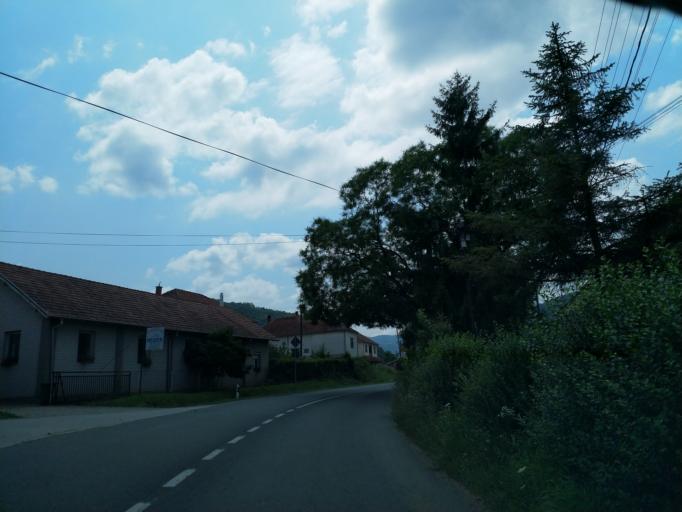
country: RS
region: Central Serbia
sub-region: Toplicki Okrug
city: Blace
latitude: 43.3485
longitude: 21.1691
